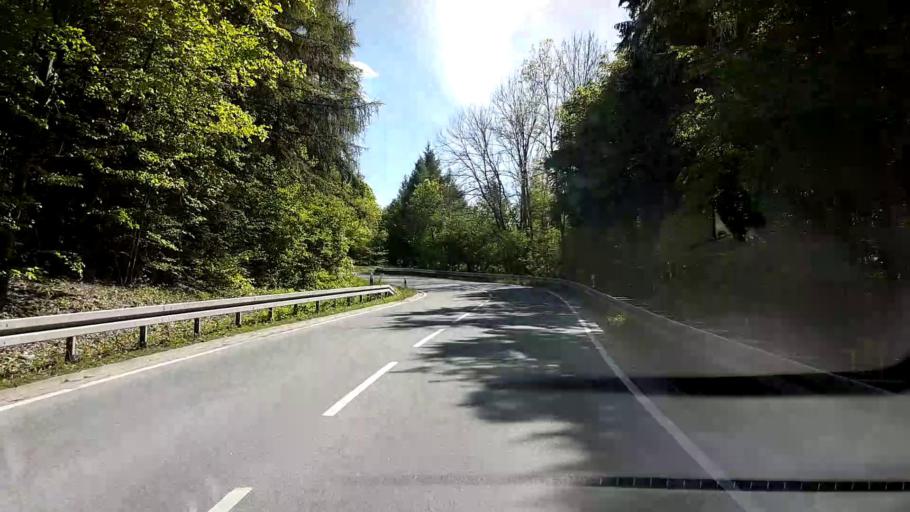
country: DE
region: Bavaria
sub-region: Upper Franconia
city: Weilersbach
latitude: 49.8077
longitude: 11.1273
